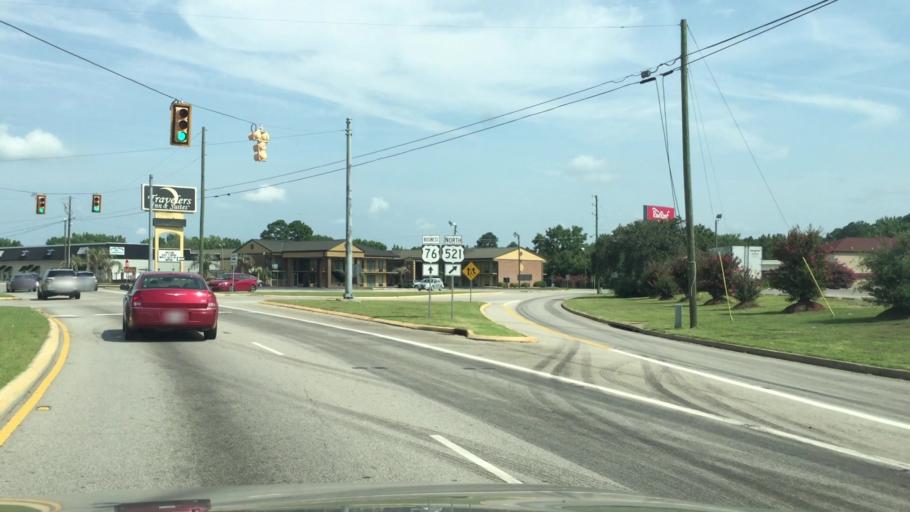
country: US
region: South Carolina
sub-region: Sumter County
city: Sumter
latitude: 33.9549
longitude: -80.3796
